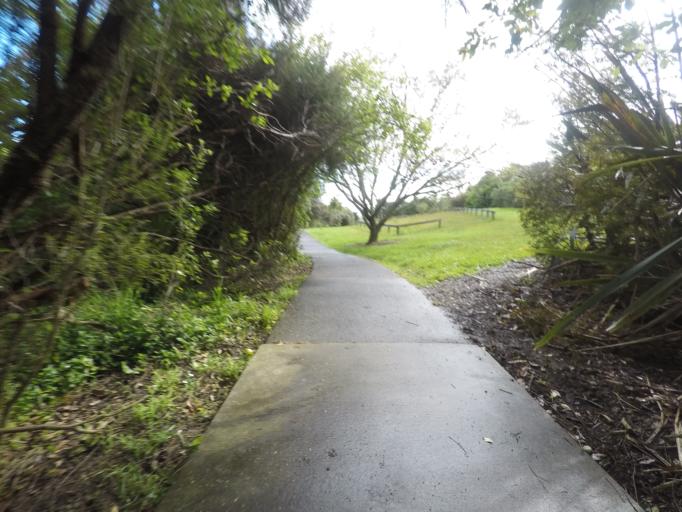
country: NZ
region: Auckland
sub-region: Auckland
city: Rosebank
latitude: -36.9025
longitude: 174.6998
